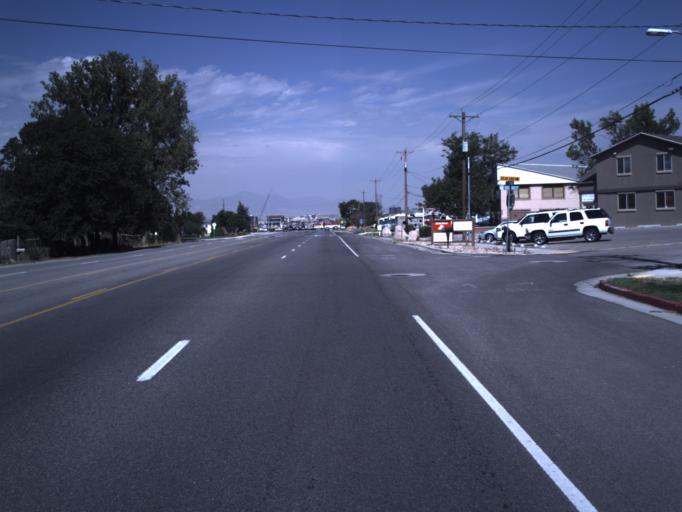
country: US
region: Utah
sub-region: Utah County
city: Lehi
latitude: 40.4090
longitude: -111.8639
